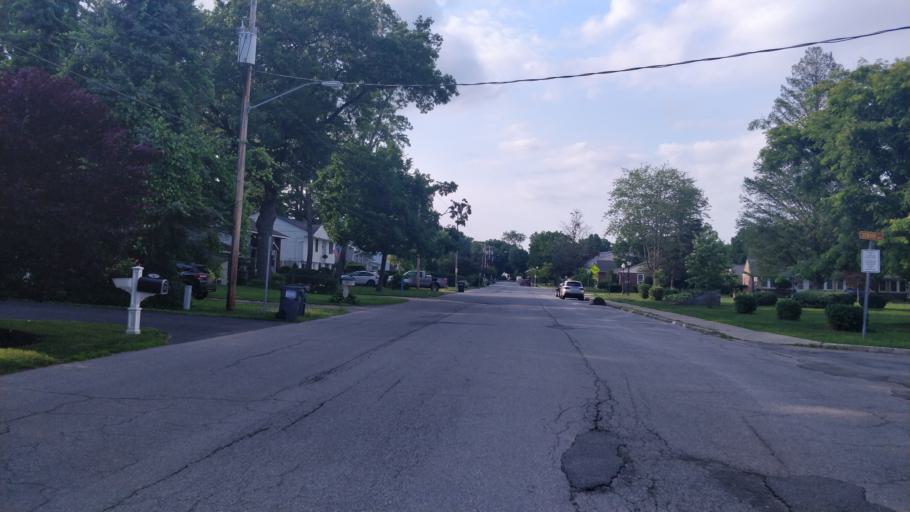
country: US
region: New York
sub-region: Saratoga County
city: Saratoga Springs
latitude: 43.0702
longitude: -73.7827
